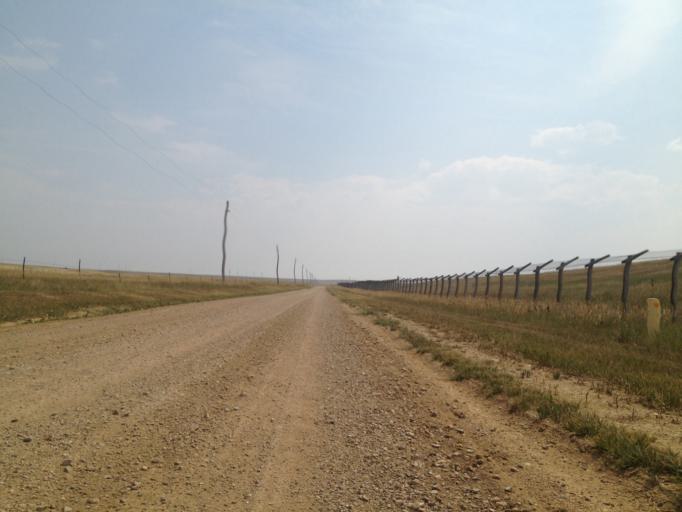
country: US
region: Colorado
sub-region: Boulder County
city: Superior
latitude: 39.9479
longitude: -105.1989
